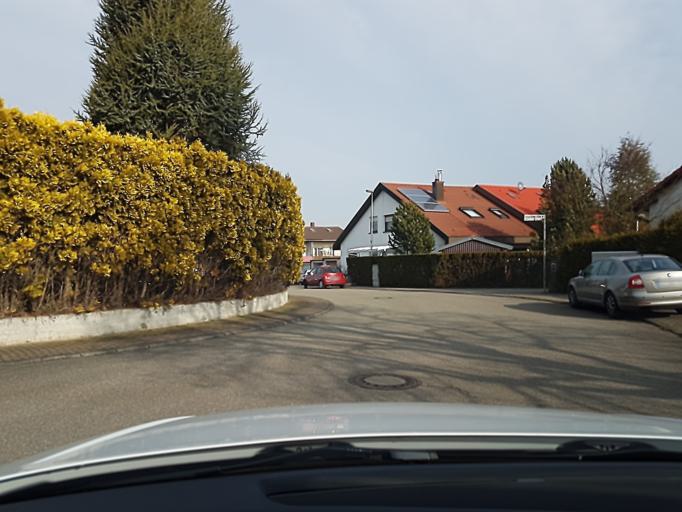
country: DE
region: Baden-Wuerttemberg
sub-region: Regierungsbezirk Stuttgart
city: Leingarten
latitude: 49.1400
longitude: 9.1309
